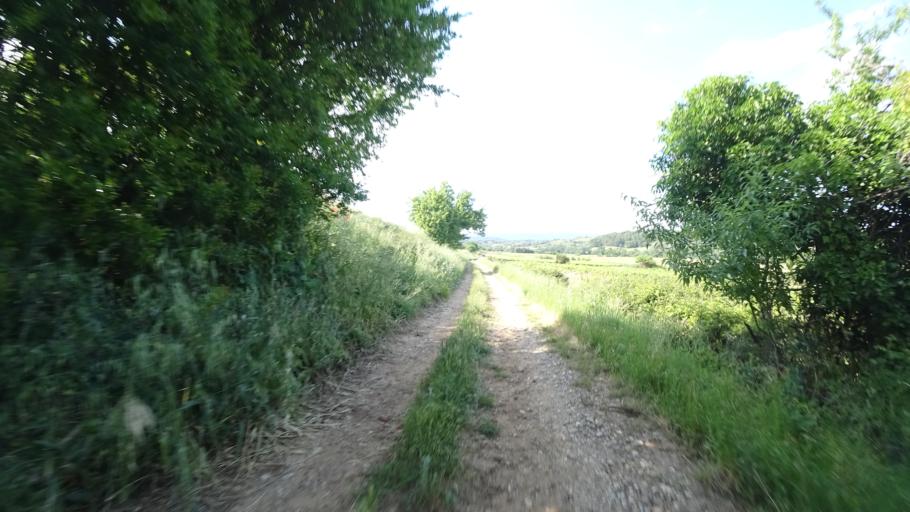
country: FR
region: Languedoc-Roussillon
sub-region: Departement de l'Aude
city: Canet
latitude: 43.2532
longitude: 2.8358
